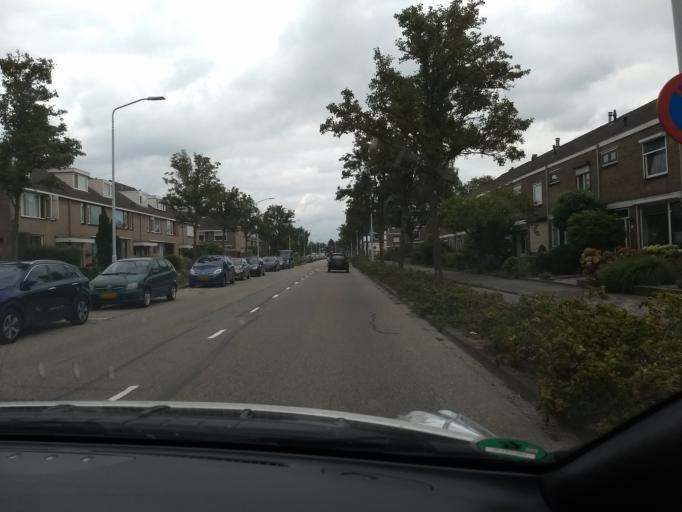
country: NL
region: South Holland
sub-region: Gemeente Papendrecht
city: Papendrecht
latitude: 51.8353
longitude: 4.6830
